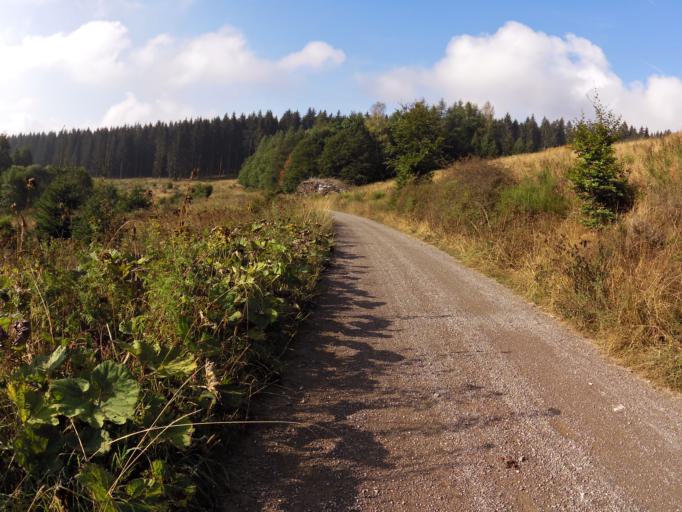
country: DE
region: North Rhine-Westphalia
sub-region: Regierungsbezirk Koln
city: Nettersheim
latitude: 50.4610
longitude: 6.6067
